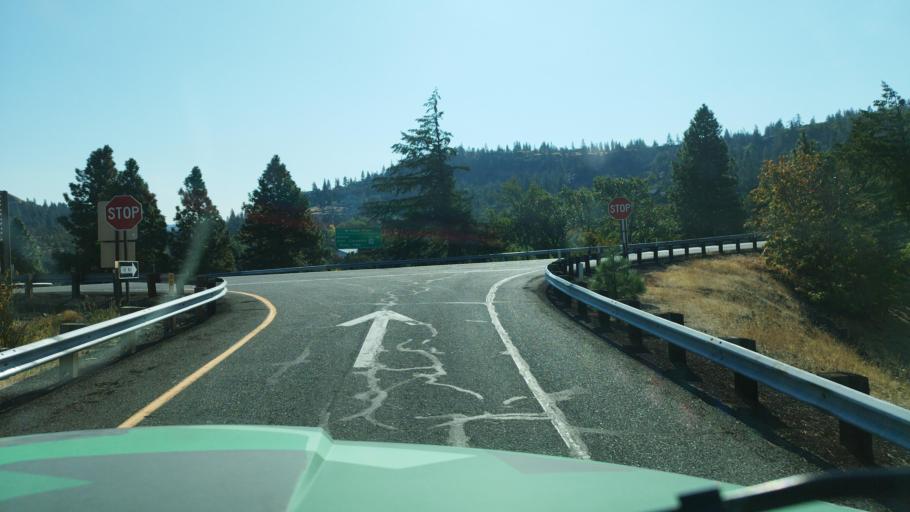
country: US
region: Washington
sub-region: Klickitat County
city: White Salmon
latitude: 45.6857
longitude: -121.4020
